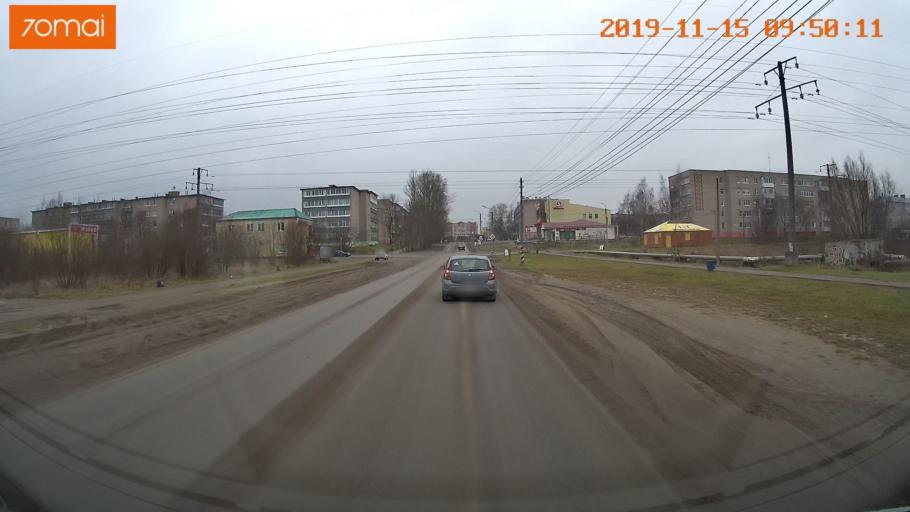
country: RU
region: Vologda
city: Sheksna
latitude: 59.2316
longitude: 38.5129
